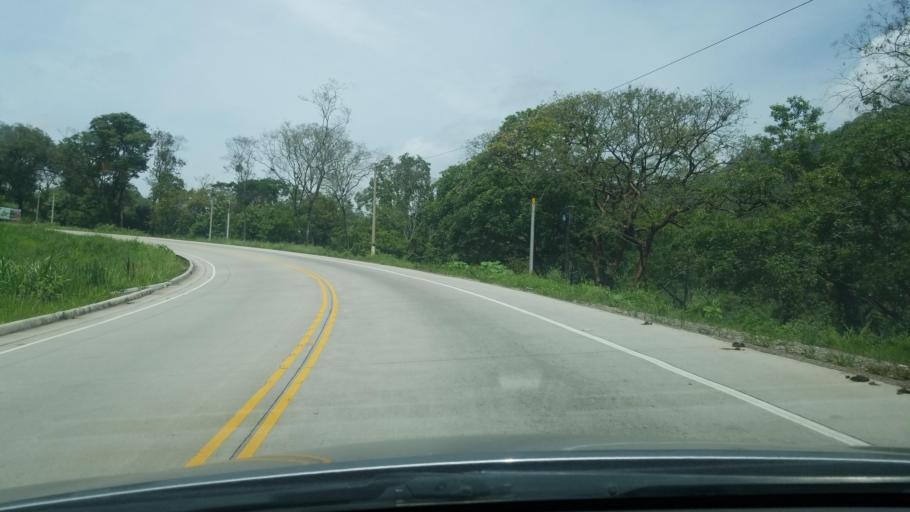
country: HN
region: Copan
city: Agua Caliente
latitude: 14.8709
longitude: -88.7839
